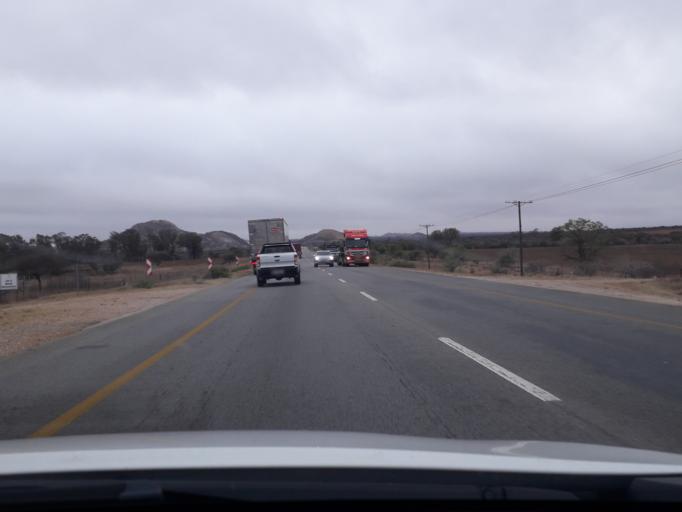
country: ZA
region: Limpopo
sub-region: Capricorn District Municipality
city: Mankoeng
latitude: -23.5471
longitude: 29.6932
